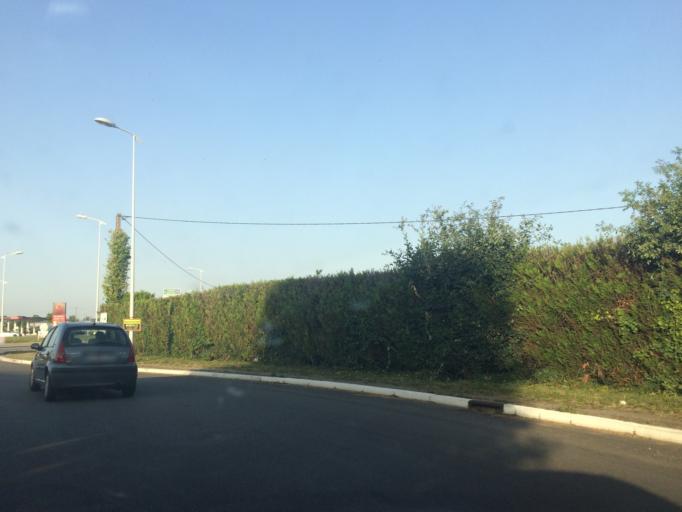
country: FR
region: Brittany
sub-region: Departement du Morbihan
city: Muzillac
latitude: 47.5587
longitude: -2.5066
